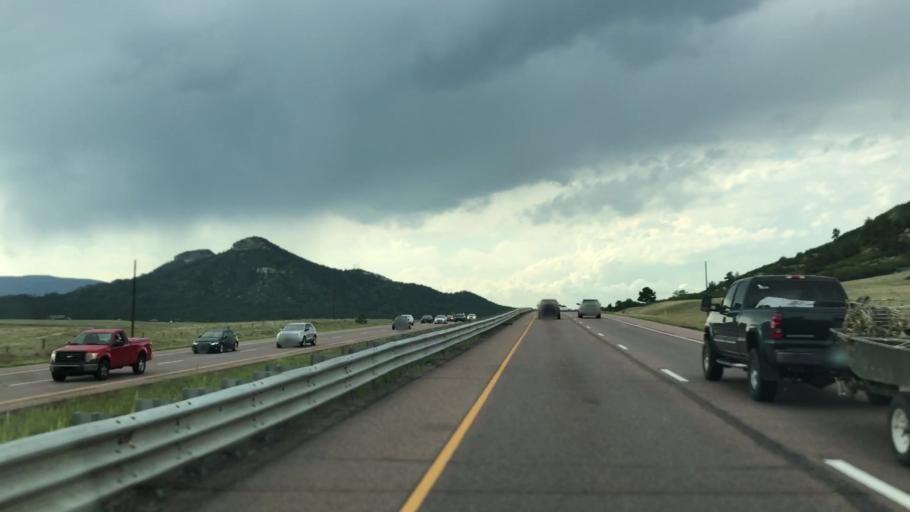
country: US
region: Colorado
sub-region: El Paso County
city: Palmer Lake
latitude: 39.2113
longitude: -104.8688
